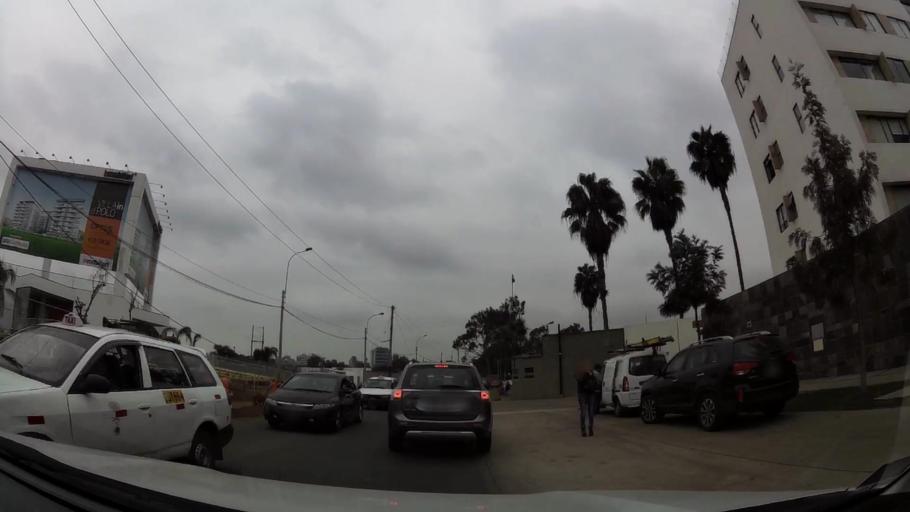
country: PE
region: Lima
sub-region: Lima
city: La Molina
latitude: -12.1022
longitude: -76.9639
